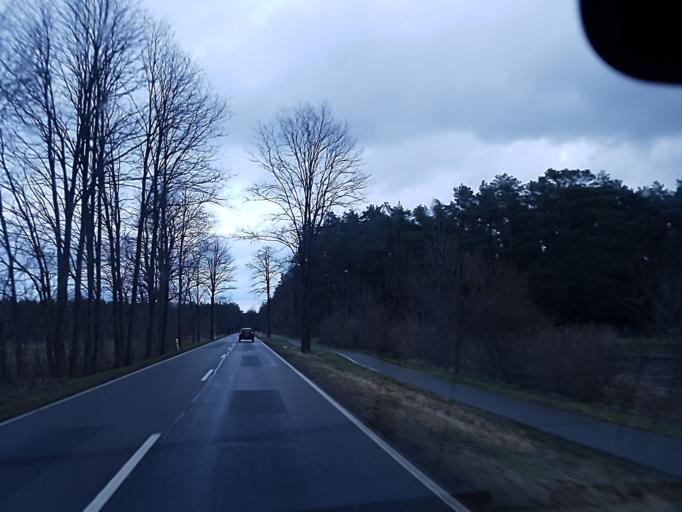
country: DE
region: Brandenburg
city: Finsterwalde
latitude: 51.5745
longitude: 13.6844
